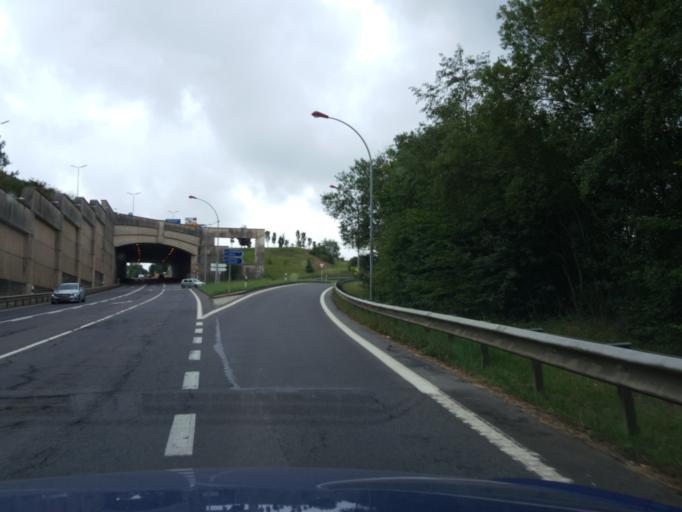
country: LU
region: Luxembourg
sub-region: Canton de Mersch
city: Mersch
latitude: 49.7643
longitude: 6.0896
